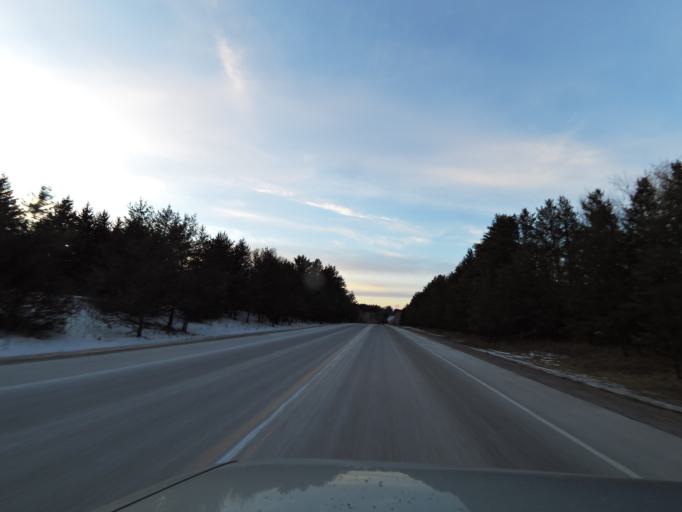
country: US
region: Minnesota
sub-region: Washington County
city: Bayport
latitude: 45.0295
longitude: -92.7492
